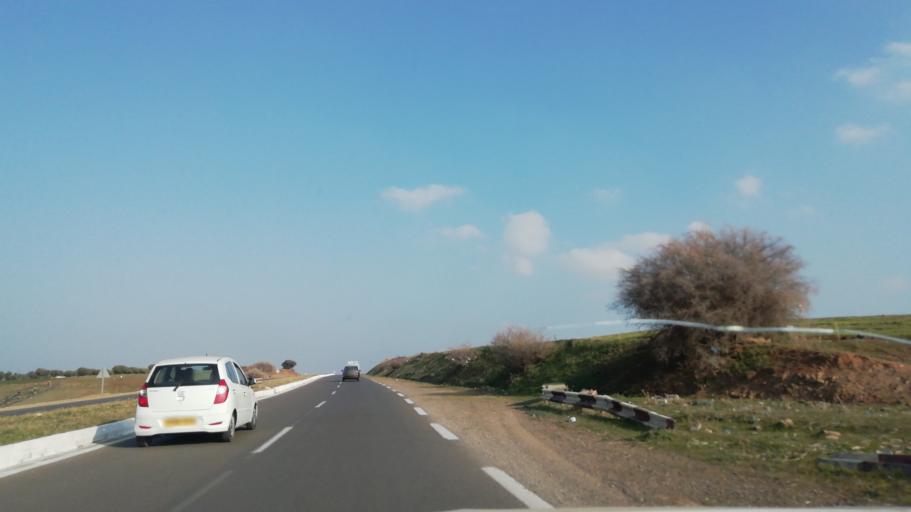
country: DZ
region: Ain Temouchent
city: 'Ain Temouchent
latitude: 35.2934
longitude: -1.1019
